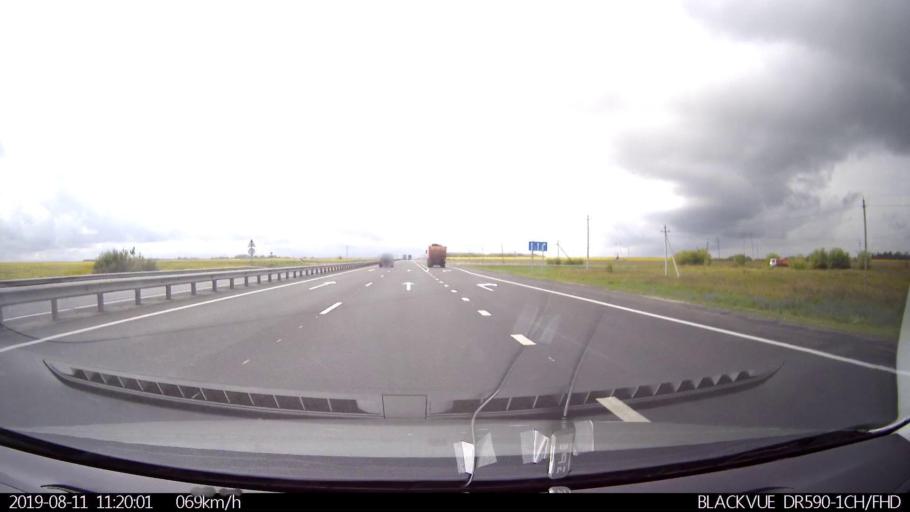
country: RU
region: Ulyanovsk
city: Novoul'yanovsk
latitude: 54.1628
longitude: 48.2646
